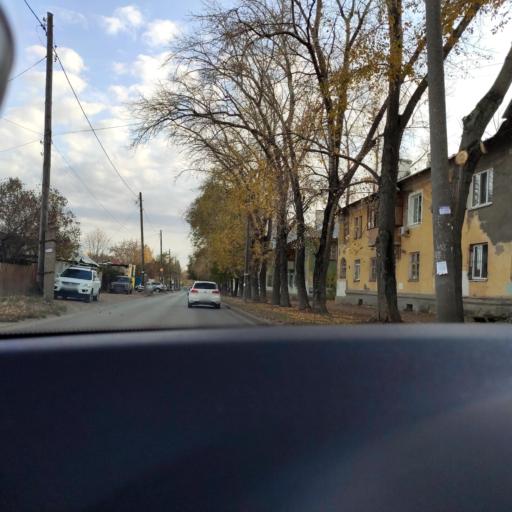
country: RU
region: Samara
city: Samara
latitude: 53.2237
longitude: 50.2466
